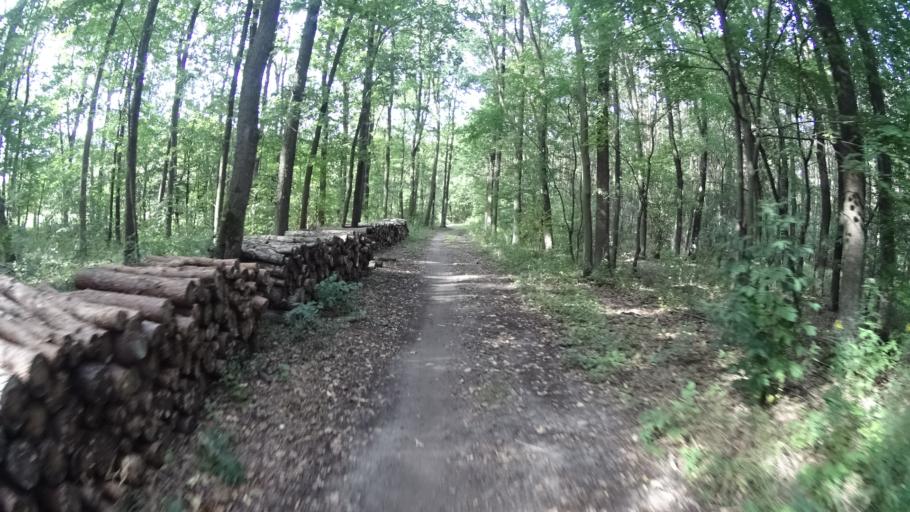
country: PL
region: Masovian Voivodeship
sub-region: Powiat warszawski zachodni
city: Babice
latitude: 52.2722
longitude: 20.8720
